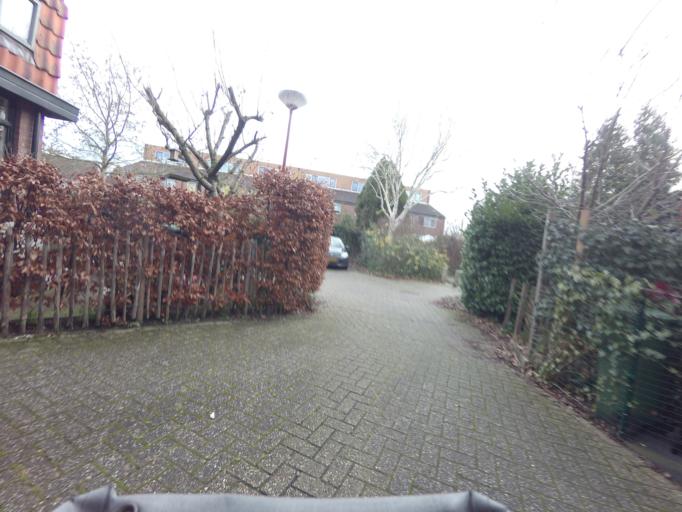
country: NL
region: Utrecht
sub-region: Gemeente Nieuwegein
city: Nieuwegein
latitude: 52.0258
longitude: 5.0714
